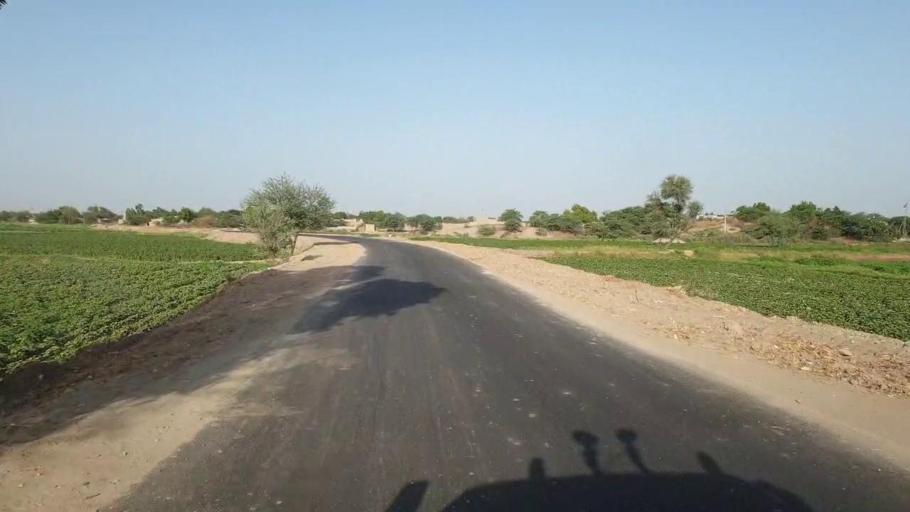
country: PK
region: Sindh
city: Jam Sahib
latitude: 26.3475
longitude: 68.5582
